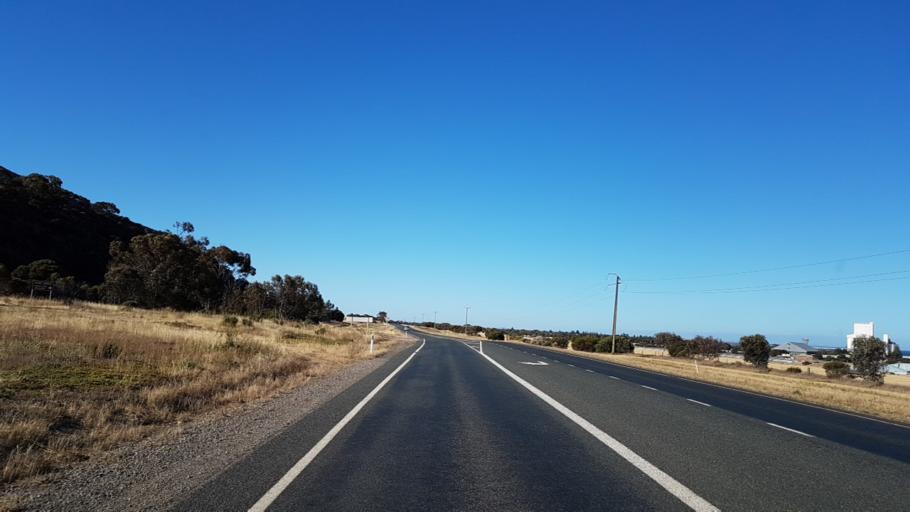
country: AU
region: South Australia
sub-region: Yorke Peninsula
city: Ardrossan
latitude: -34.4466
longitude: 137.9036
